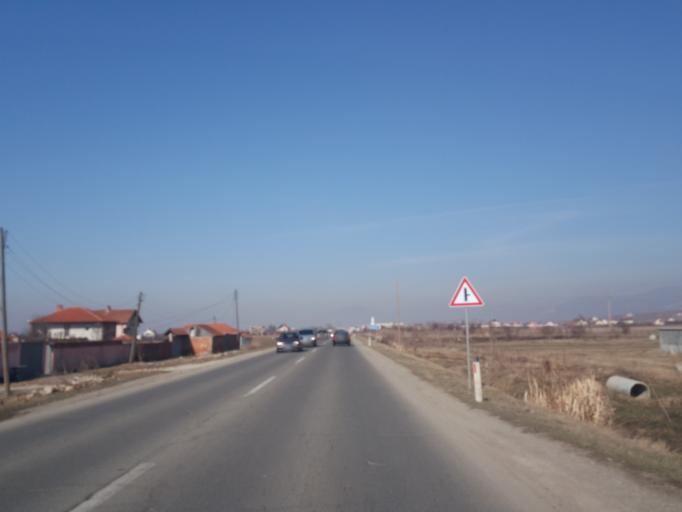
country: XK
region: Mitrovica
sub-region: Vushtrri
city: Vushtrri
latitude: 42.7933
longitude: 21.0020
